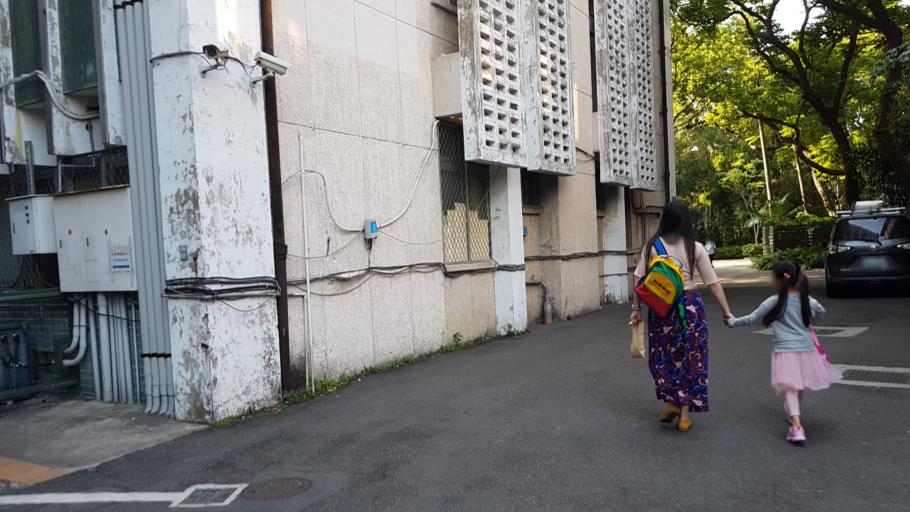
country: TW
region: Taipei
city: Taipei
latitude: 25.0146
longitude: 121.5368
